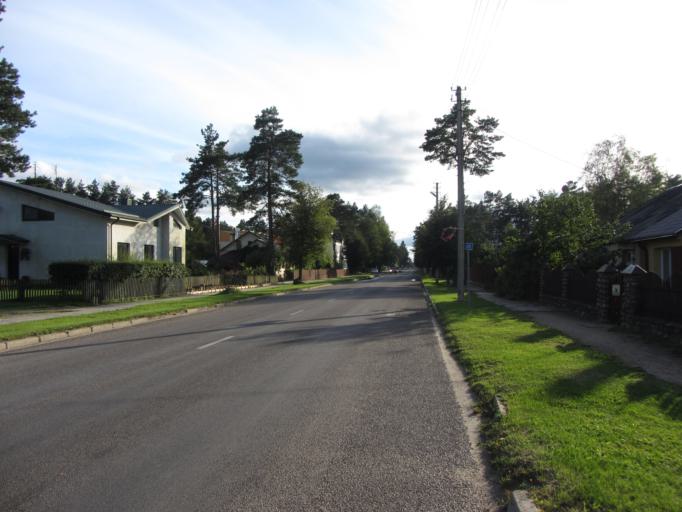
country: LT
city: Baltoji Voke
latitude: 54.4558
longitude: 25.1265
